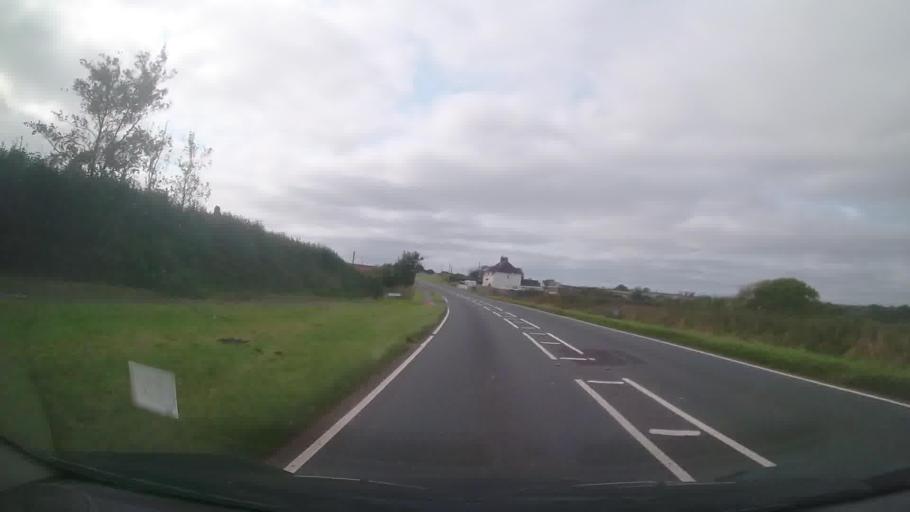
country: GB
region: Wales
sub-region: Pembrokeshire
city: Neyland
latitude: 51.7252
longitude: -4.9732
